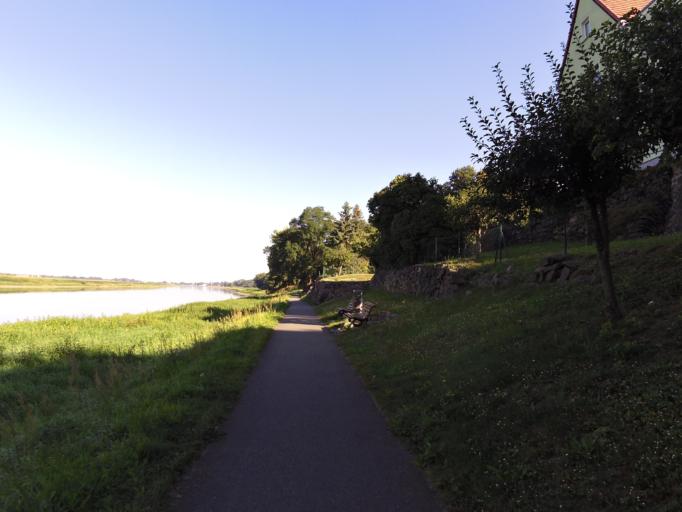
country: DE
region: Saxony
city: Nunchritz
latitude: 51.2747
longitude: 13.4049
